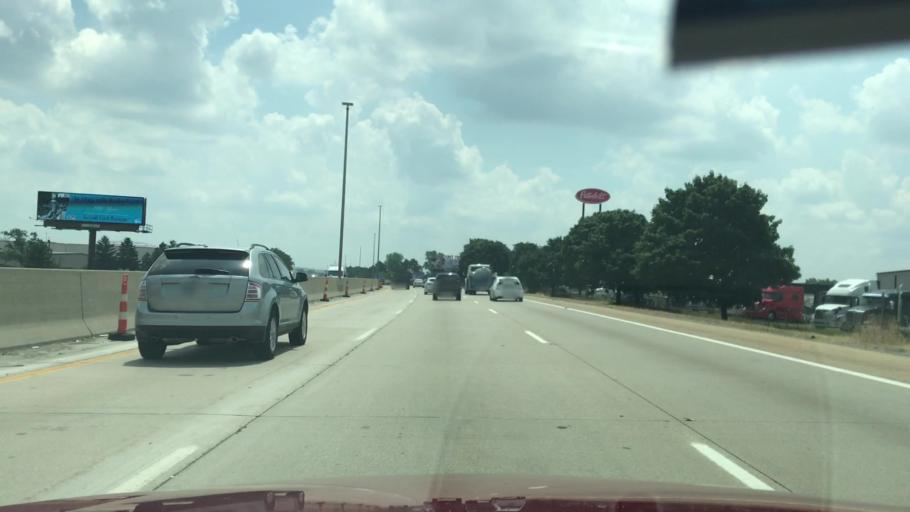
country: US
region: Michigan
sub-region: Kent County
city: Kentwood
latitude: 42.8780
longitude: -85.6822
